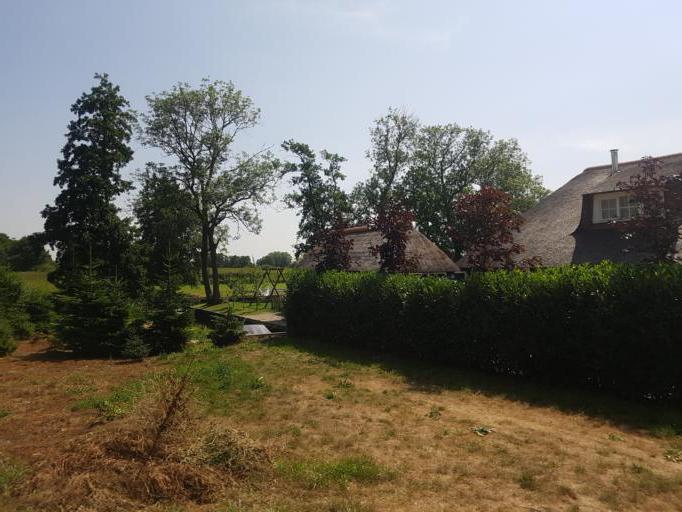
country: NL
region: Overijssel
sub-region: Gemeente Steenwijkerland
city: Giethoorn
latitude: 52.7554
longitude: 6.0827
